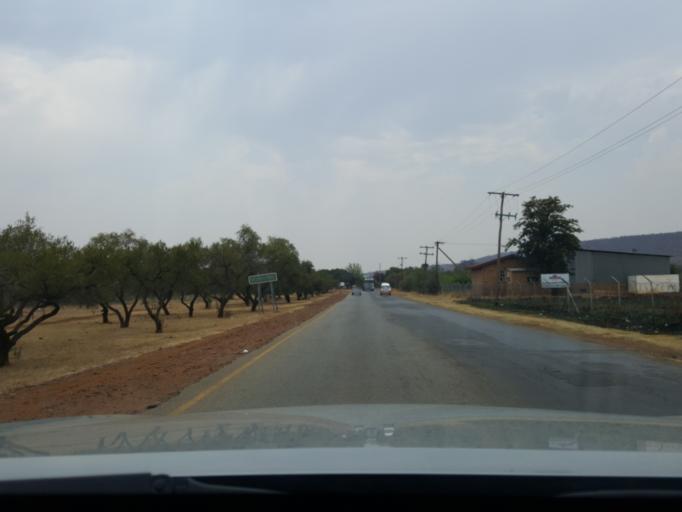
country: ZA
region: North-West
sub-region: Ngaka Modiri Molema District Municipality
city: Zeerust
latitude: -25.5018
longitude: 25.9839
